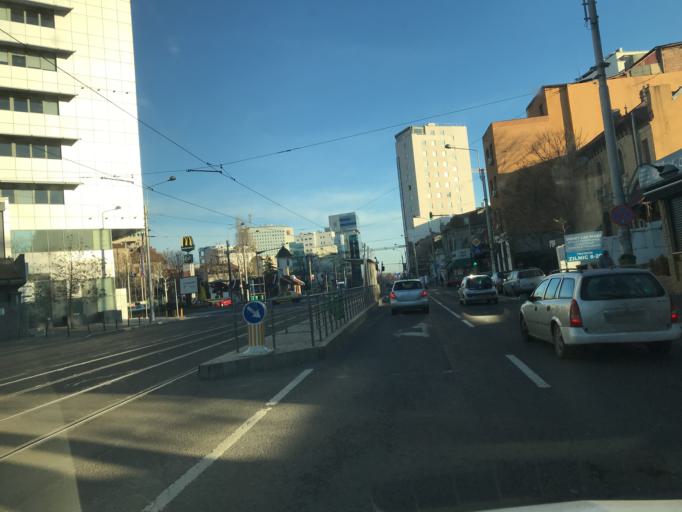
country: RO
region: Bucuresti
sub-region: Municipiul Bucuresti
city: Bucuresti
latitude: 44.4474
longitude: 26.0822
